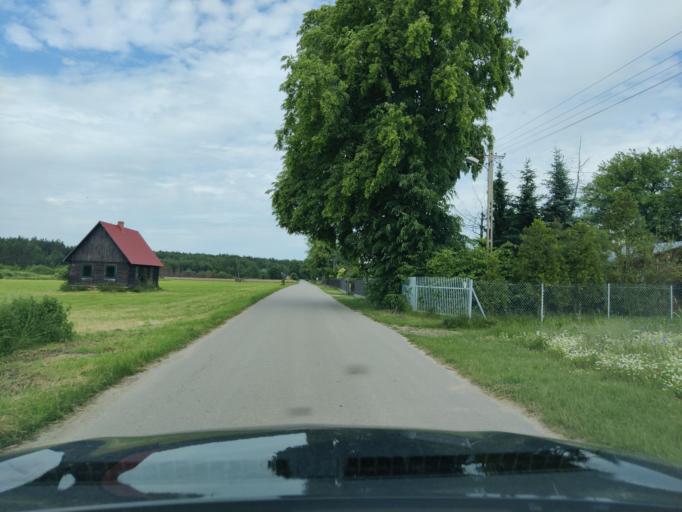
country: PL
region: Masovian Voivodeship
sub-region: Powiat pultuski
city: Obryte
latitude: 52.7347
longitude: 21.1688
